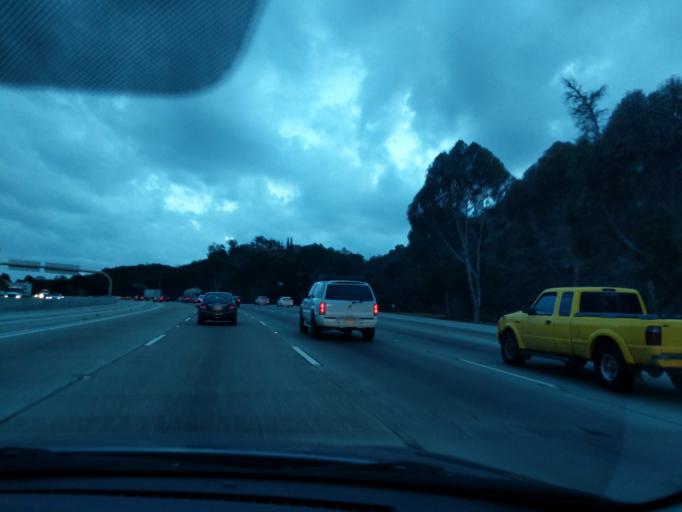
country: US
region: California
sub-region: San Diego County
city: San Diego
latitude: 32.7736
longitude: -117.1125
